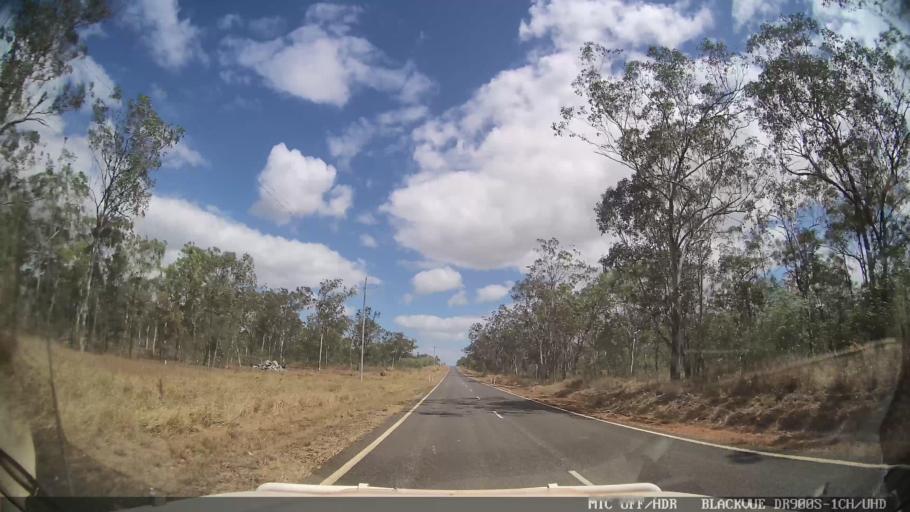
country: AU
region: Queensland
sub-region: Tablelands
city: Ravenshoe
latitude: -17.7268
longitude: 145.0479
